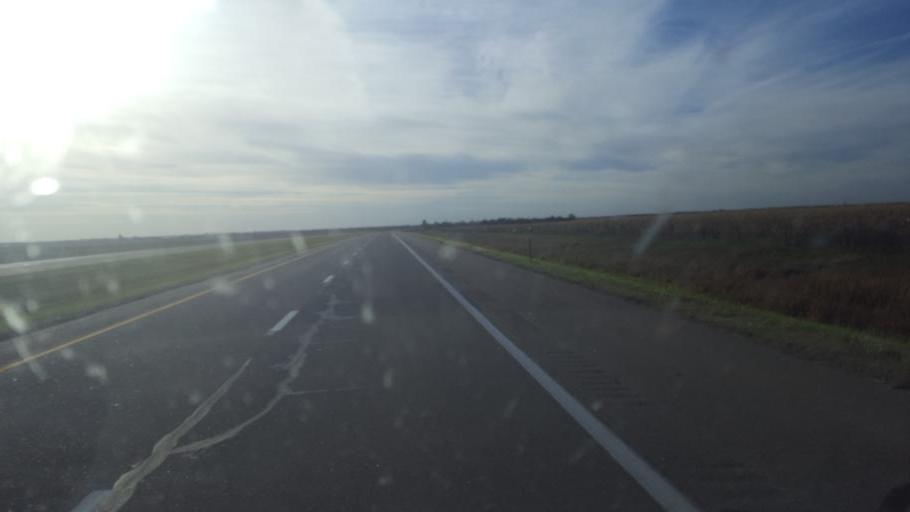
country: US
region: Kansas
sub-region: Trego County
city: WaKeeney
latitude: 39.0240
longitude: -100.1496
